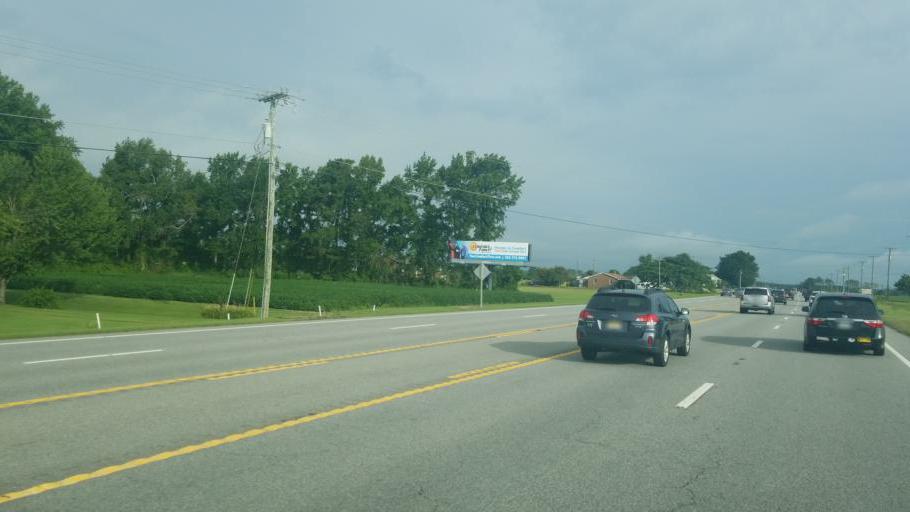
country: US
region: North Carolina
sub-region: Currituck County
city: Currituck
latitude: 36.3933
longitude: -75.9808
